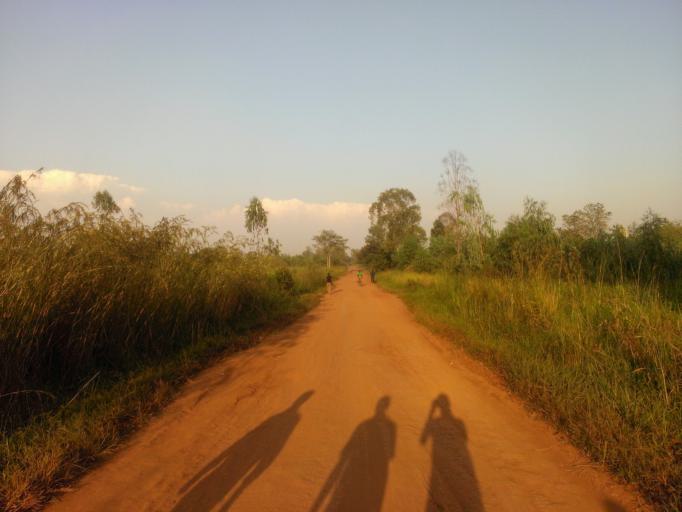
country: UG
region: Northern Region
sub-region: Gulu District
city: Gulu
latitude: 2.7813
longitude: 32.3092
